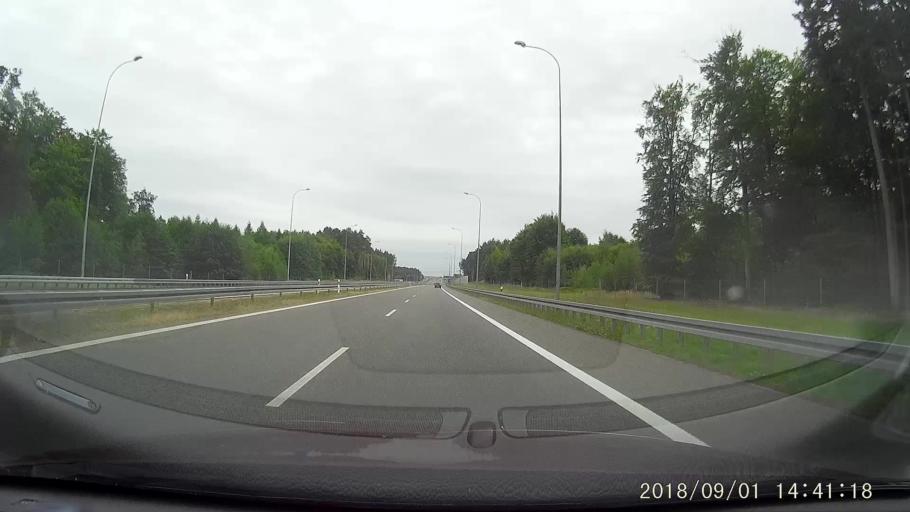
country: PL
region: Lubusz
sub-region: Powiat gorzowski
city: Jenin
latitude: 52.7939
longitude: 15.1144
